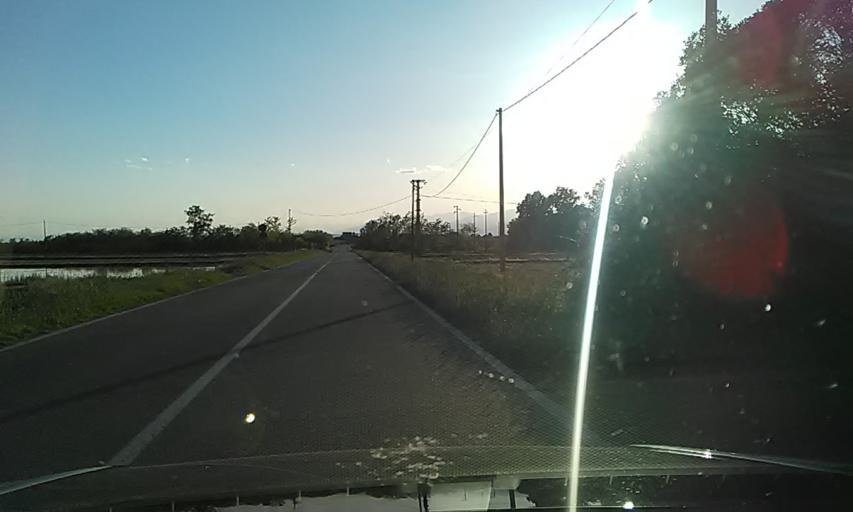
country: IT
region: Piedmont
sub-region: Provincia di Vercelli
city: San Giacomo Vercellese
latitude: 45.5219
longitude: 8.3496
